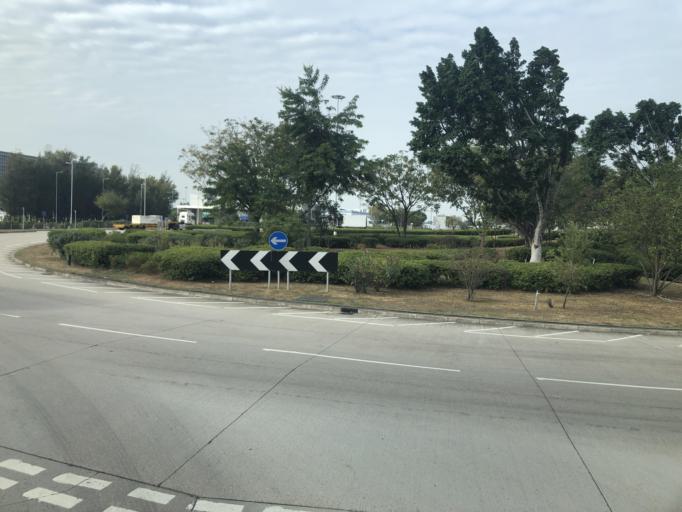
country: HK
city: Tai O
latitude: 22.2983
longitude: 113.9329
